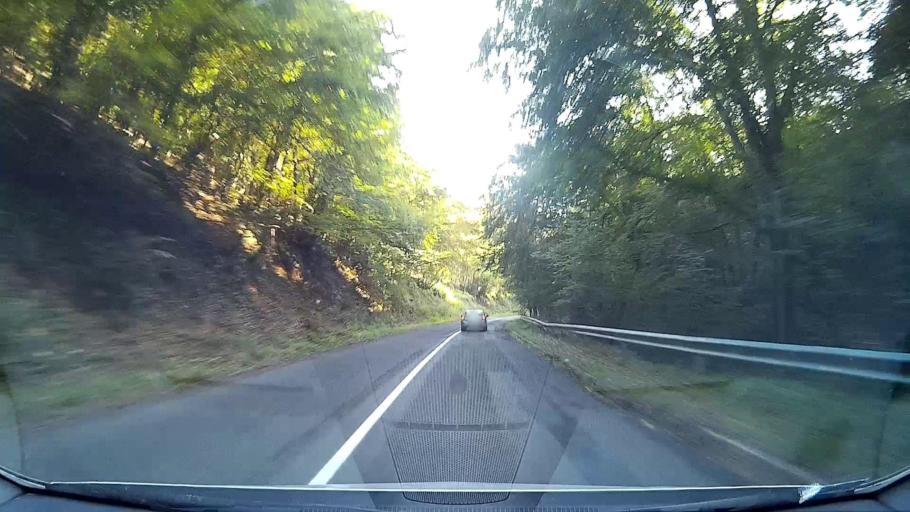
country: HU
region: Pest
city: Visegrad
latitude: 47.7540
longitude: 18.9435
